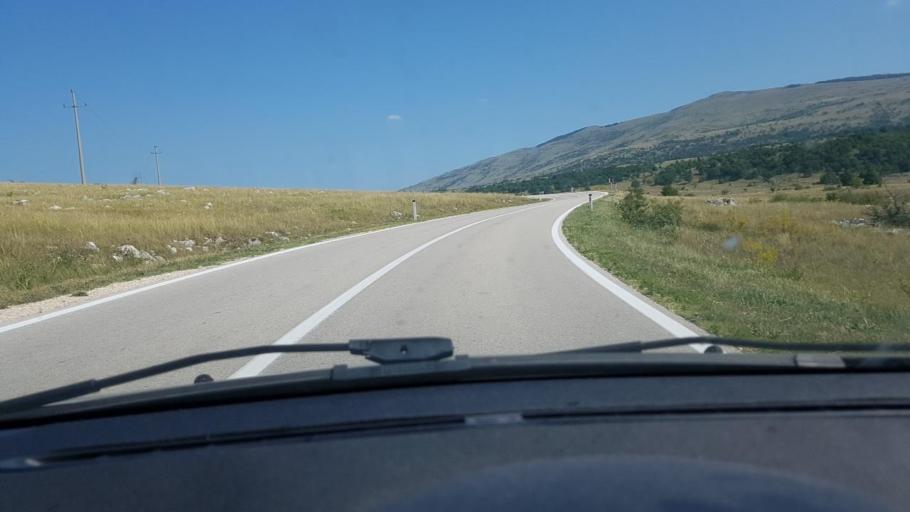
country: BA
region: Federation of Bosnia and Herzegovina
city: Bosansko Grahovo
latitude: 44.1342
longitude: 16.4763
